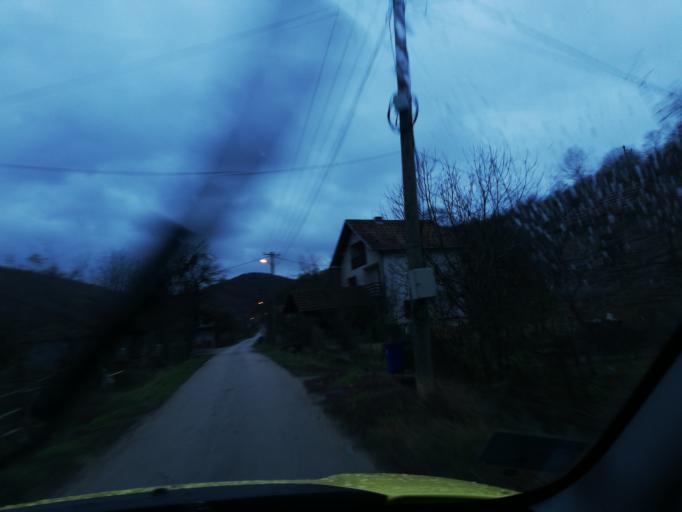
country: RS
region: Central Serbia
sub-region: Pirotski Okrug
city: Dimitrovgrad
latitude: 43.0116
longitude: 22.7214
